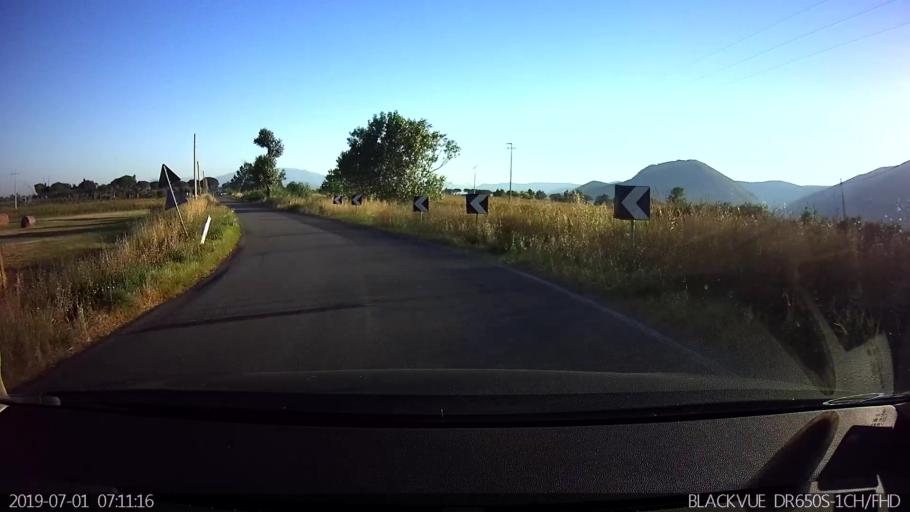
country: IT
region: Latium
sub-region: Provincia di Latina
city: Borgo Hermada
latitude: 41.3187
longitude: 13.1790
